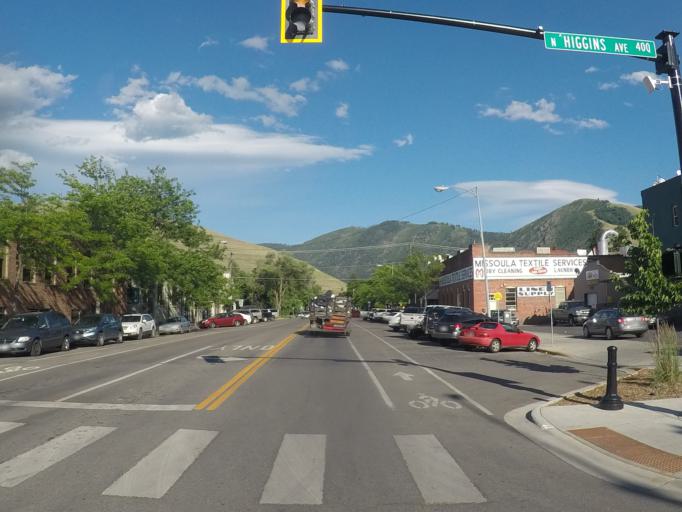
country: US
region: Montana
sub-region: Missoula County
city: Missoula
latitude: 46.8740
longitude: -113.9928
